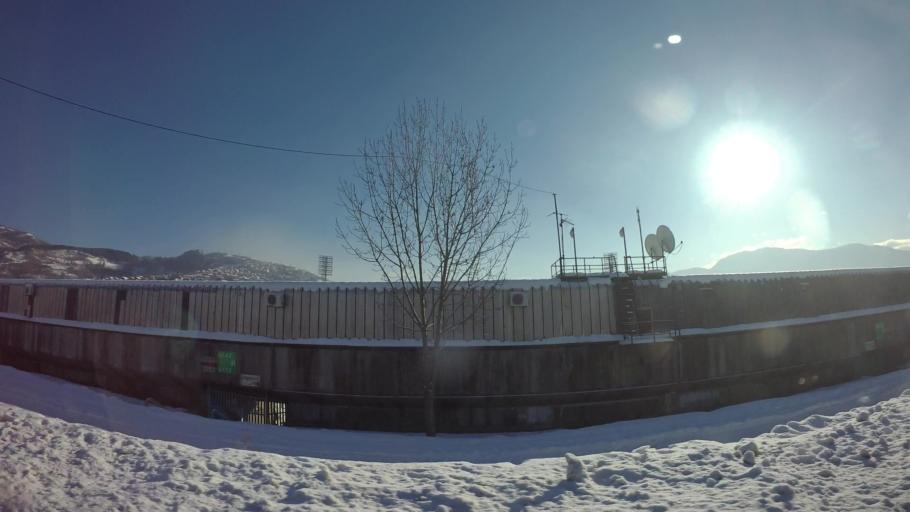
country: BA
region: Federation of Bosnia and Herzegovina
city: Kobilja Glava
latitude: 43.8742
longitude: 18.4072
